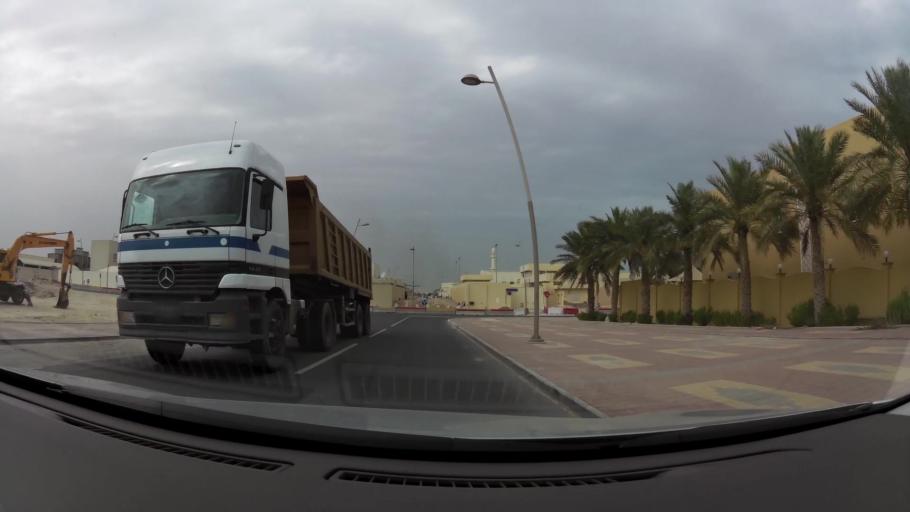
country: QA
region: Baladiyat ad Dawhah
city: Doha
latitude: 25.3433
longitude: 51.4879
